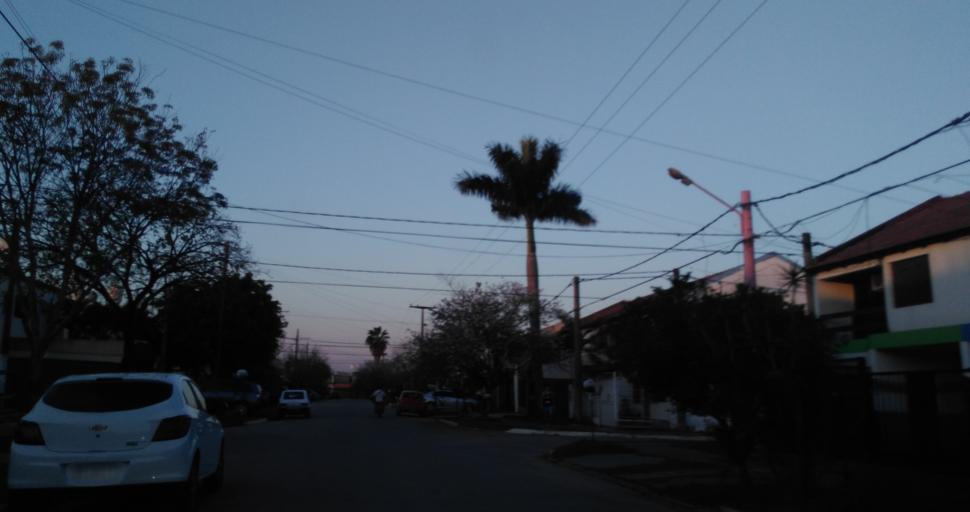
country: AR
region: Chaco
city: Resistencia
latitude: -27.4414
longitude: -58.9651
